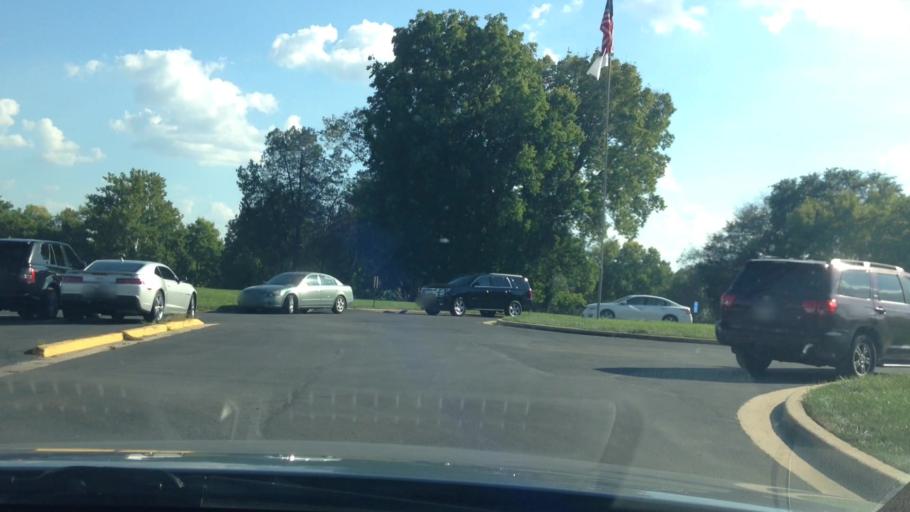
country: US
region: Kansas
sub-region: Johnson County
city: Leawood
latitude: 38.9772
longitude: -94.5822
